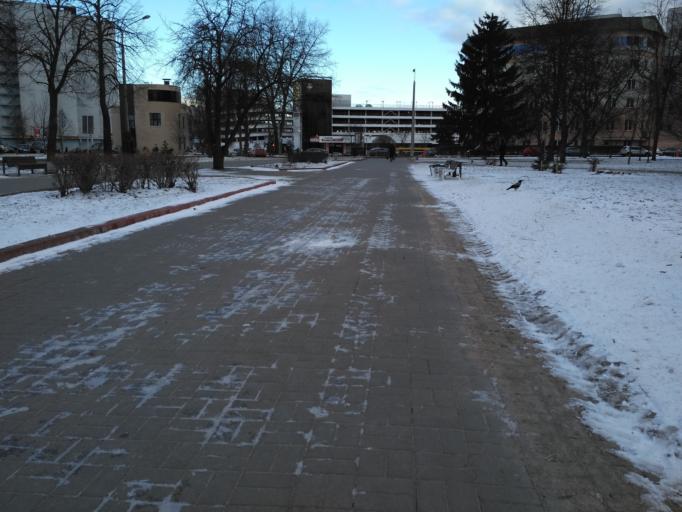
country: BY
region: Minsk
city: Minsk
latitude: 53.9231
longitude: 27.5767
